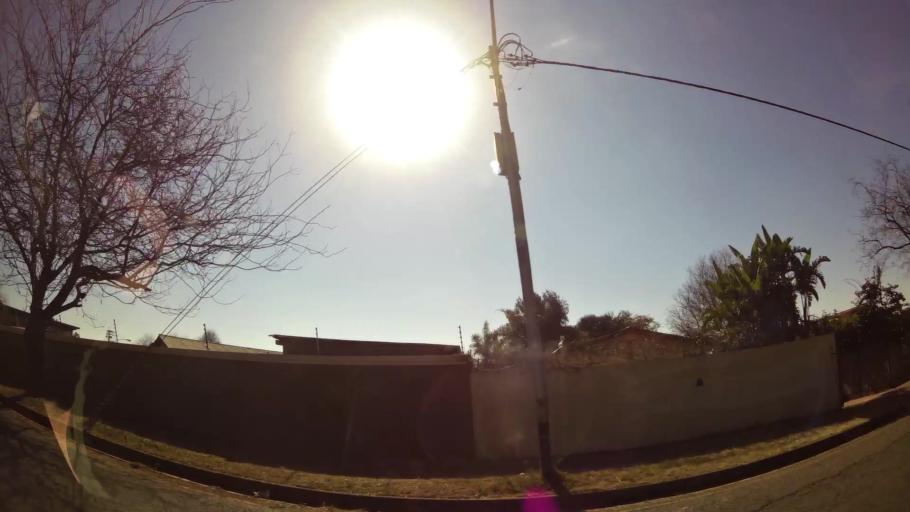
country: ZA
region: Gauteng
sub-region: City of Johannesburg Metropolitan Municipality
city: Roodepoort
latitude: -26.1787
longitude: 27.9564
